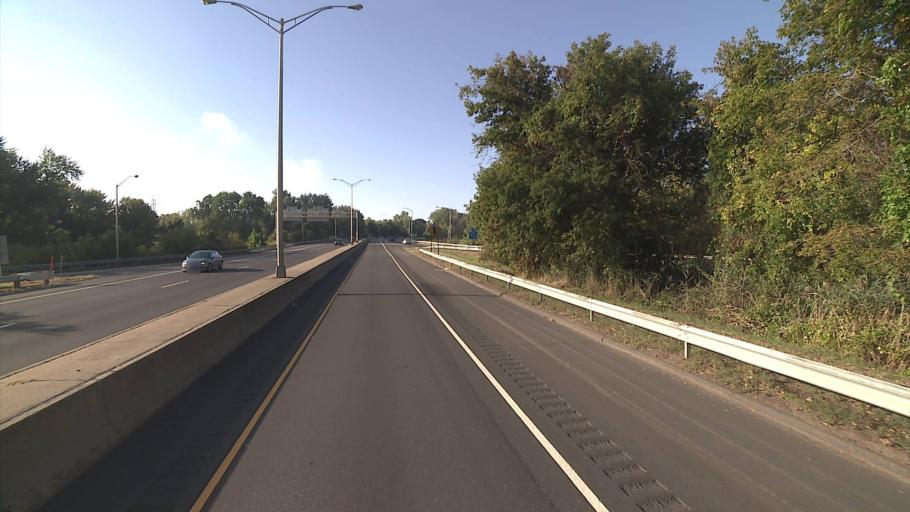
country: US
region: Connecticut
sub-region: Hartford County
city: Wethersfield
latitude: 41.7312
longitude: -72.6644
